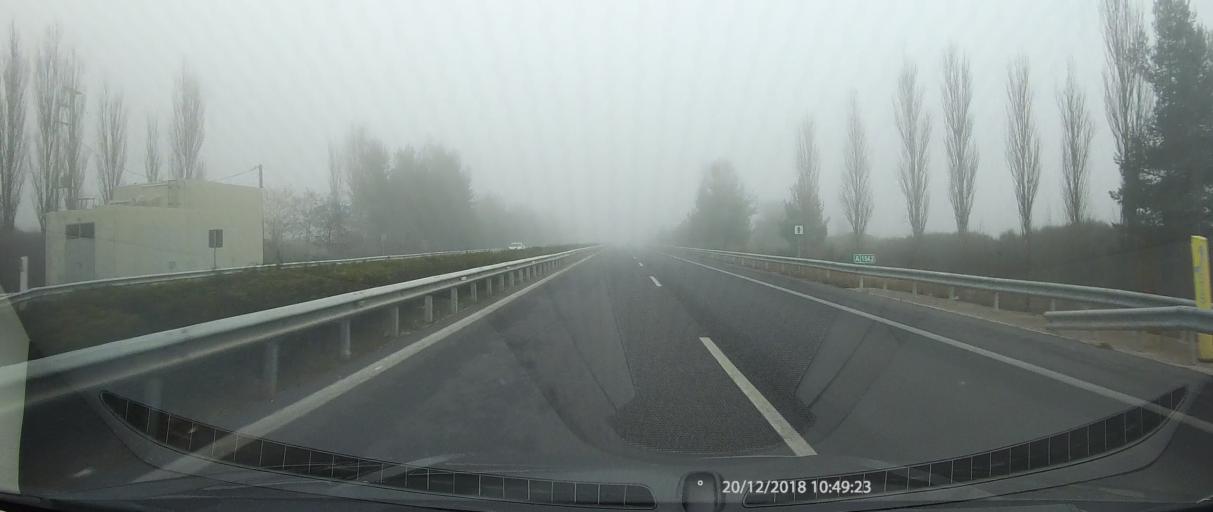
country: GR
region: Peloponnese
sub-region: Nomos Arkadias
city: Tripoli
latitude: 37.5381
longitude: 22.4145
